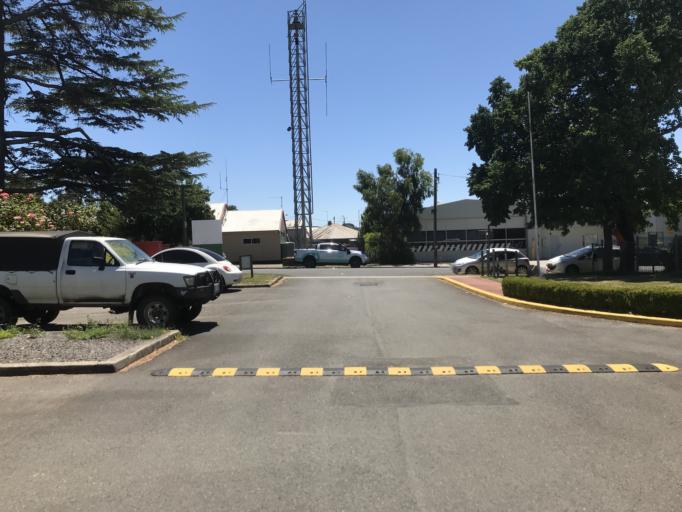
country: AU
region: Victoria
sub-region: Ballarat North
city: Delacombe
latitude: -37.4308
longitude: 143.3821
